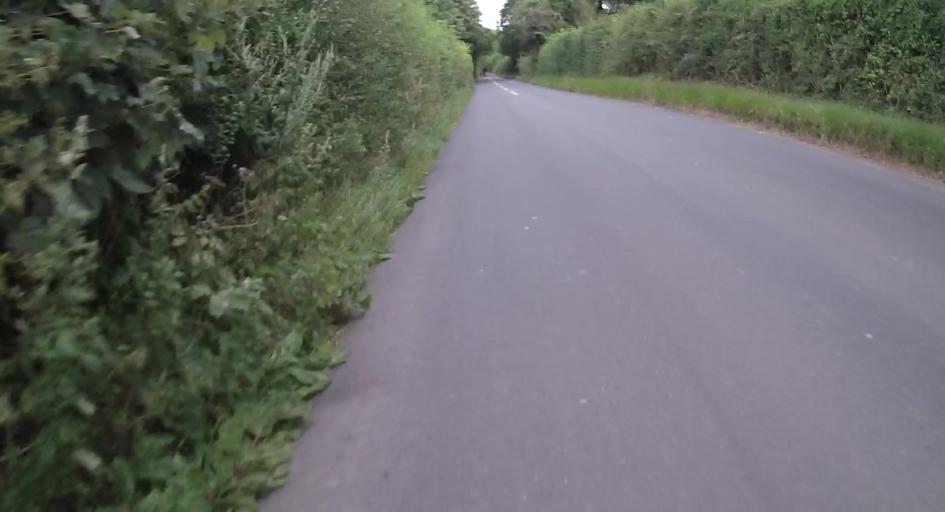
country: GB
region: England
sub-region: Hampshire
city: Kings Worthy
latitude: 51.1276
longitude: -1.3100
